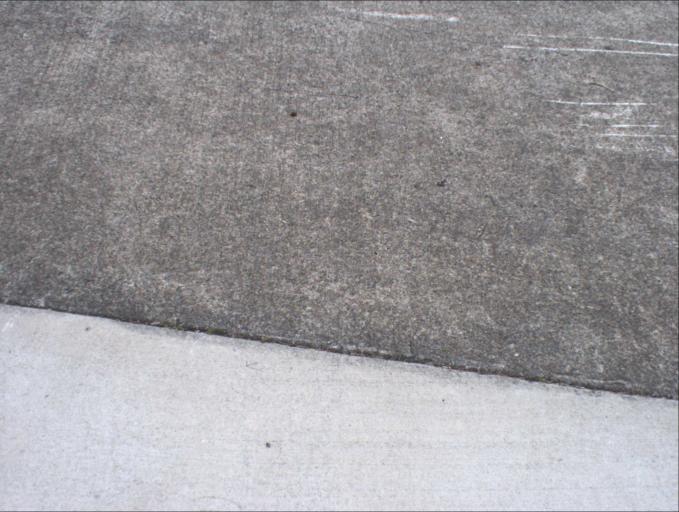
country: AU
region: Queensland
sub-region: Logan
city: Logan Reserve
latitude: -27.7146
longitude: 153.1155
